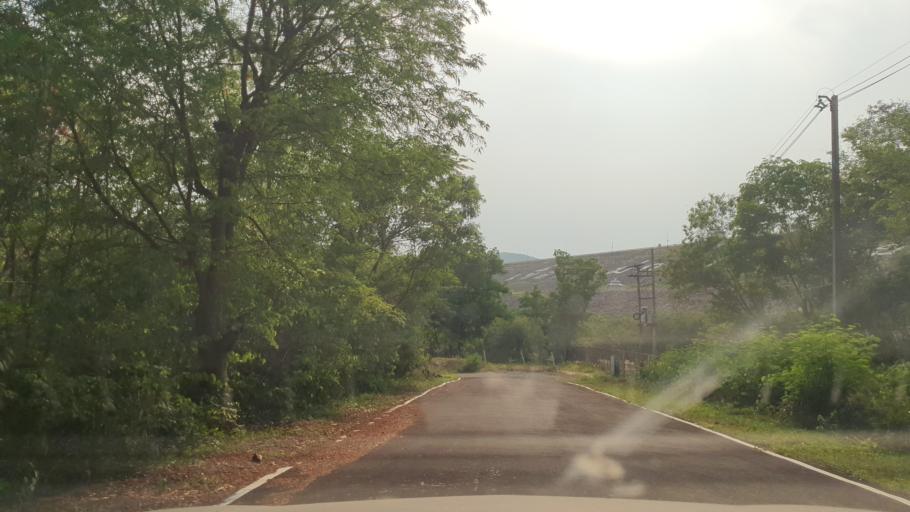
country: TH
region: Chiang Mai
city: San Sai
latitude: 18.9259
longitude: 99.1285
